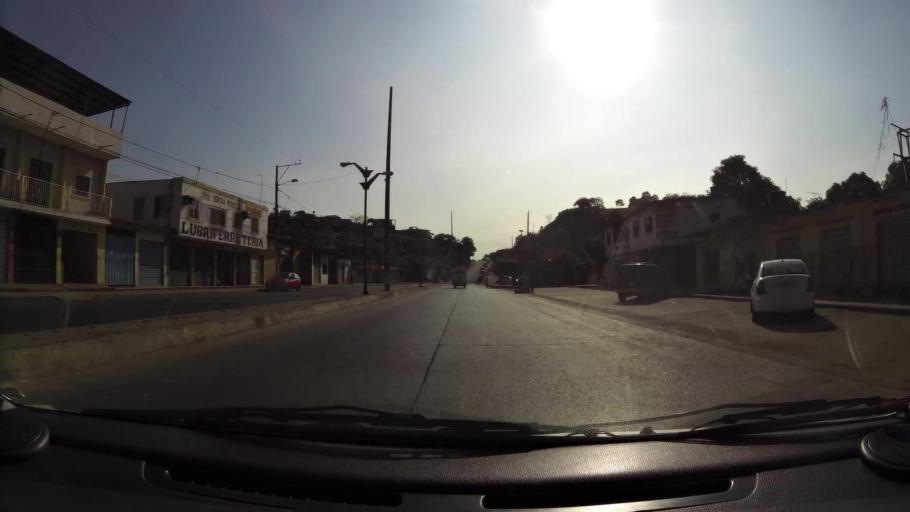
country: EC
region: Guayas
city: Eloy Alfaro
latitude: -2.1745
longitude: -79.8468
